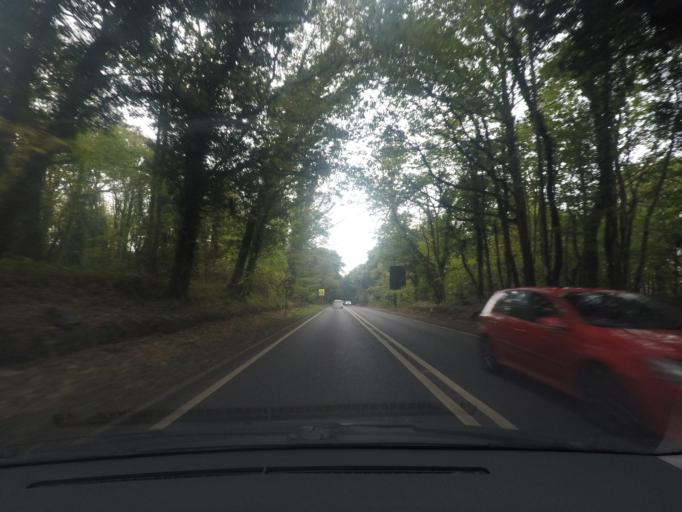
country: GB
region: England
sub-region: Sheffield
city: Chapletown
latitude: 53.4642
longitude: -1.5043
